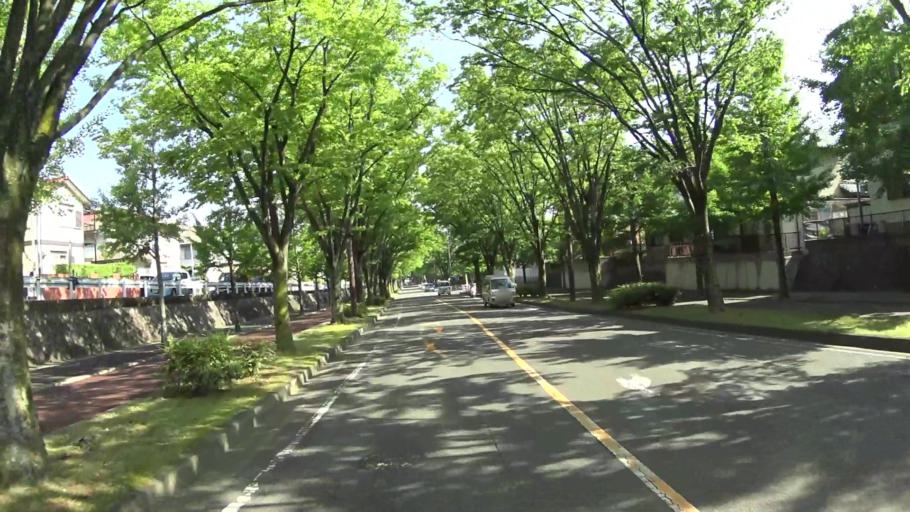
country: JP
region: Kyoto
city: Muko
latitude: 34.9587
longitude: 135.6697
